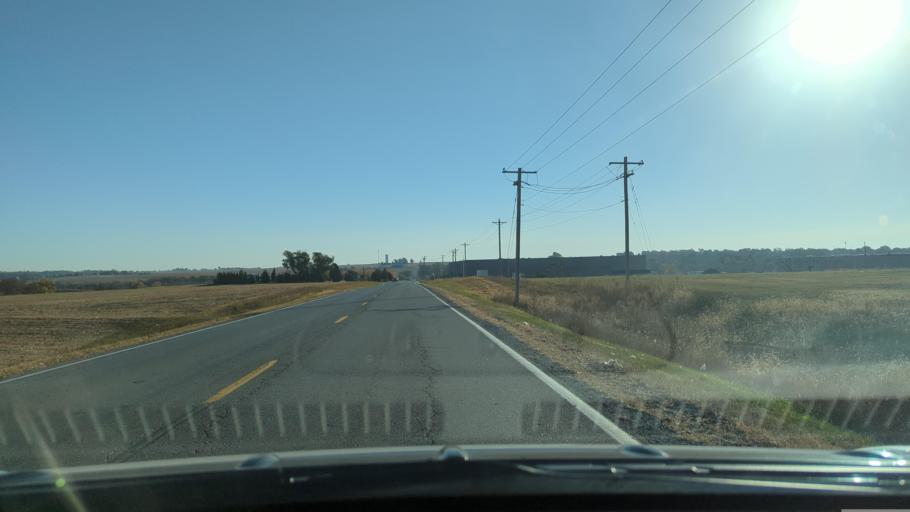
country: US
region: Nebraska
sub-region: Sarpy County
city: Springfield
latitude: 41.0892
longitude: -96.1473
